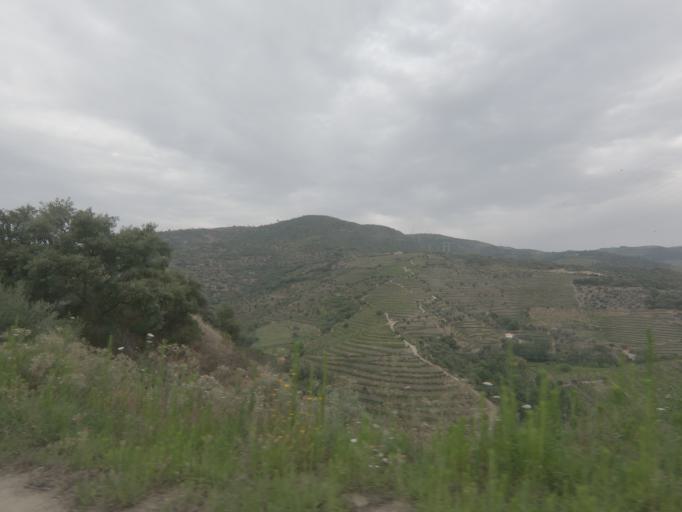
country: PT
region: Viseu
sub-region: Armamar
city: Armamar
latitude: 41.1425
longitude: -7.6446
